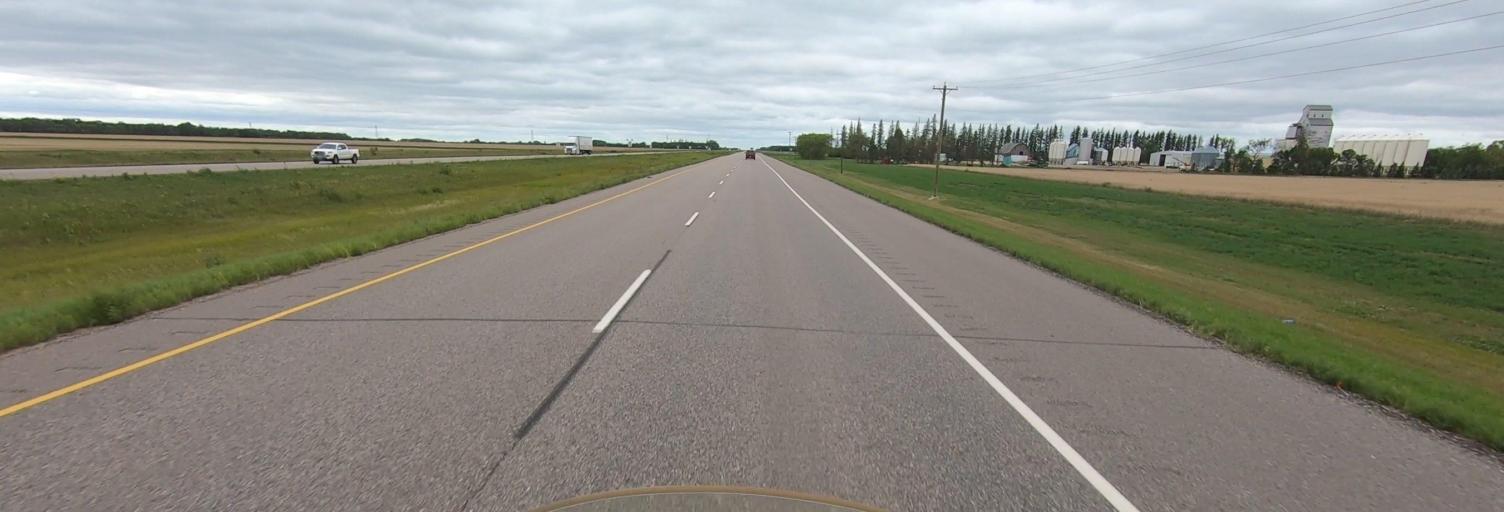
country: CA
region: Manitoba
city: Portage la Prairie
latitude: 49.9752
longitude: -98.5075
